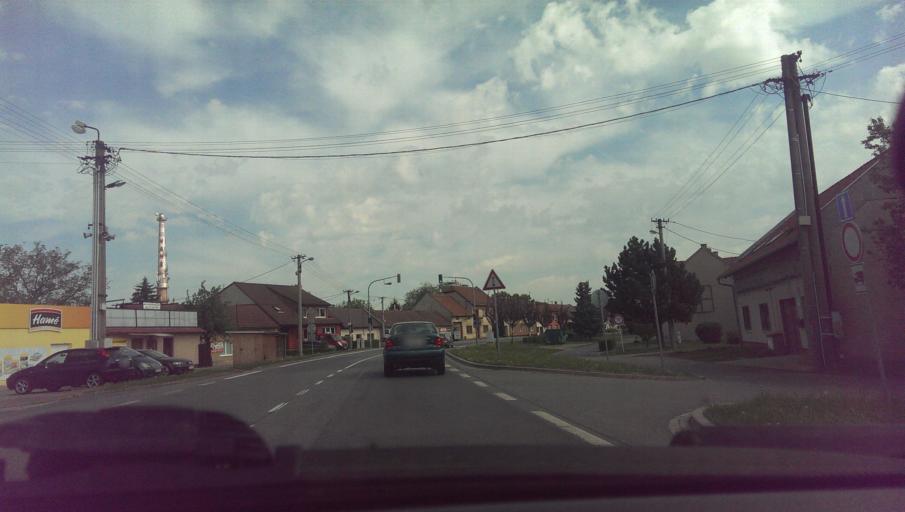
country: CZ
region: Zlin
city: Babice
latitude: 49.1180
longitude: 17.4708
